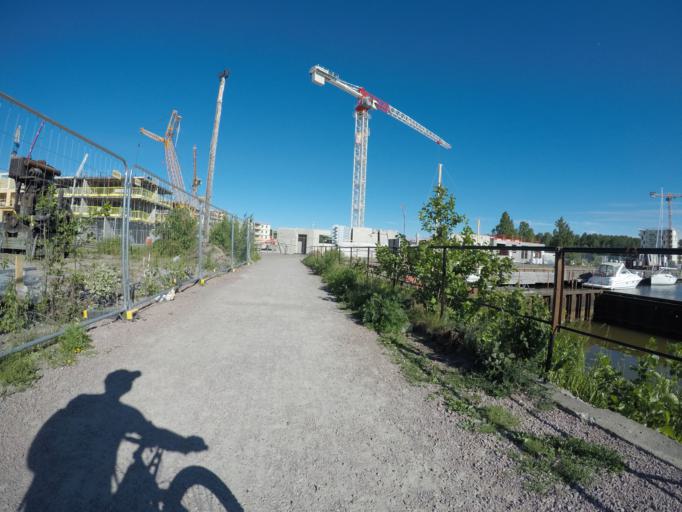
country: SE
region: Vaestmanland
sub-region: Vasteras
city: Vasteras
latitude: 59.6062
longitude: 16.5689
